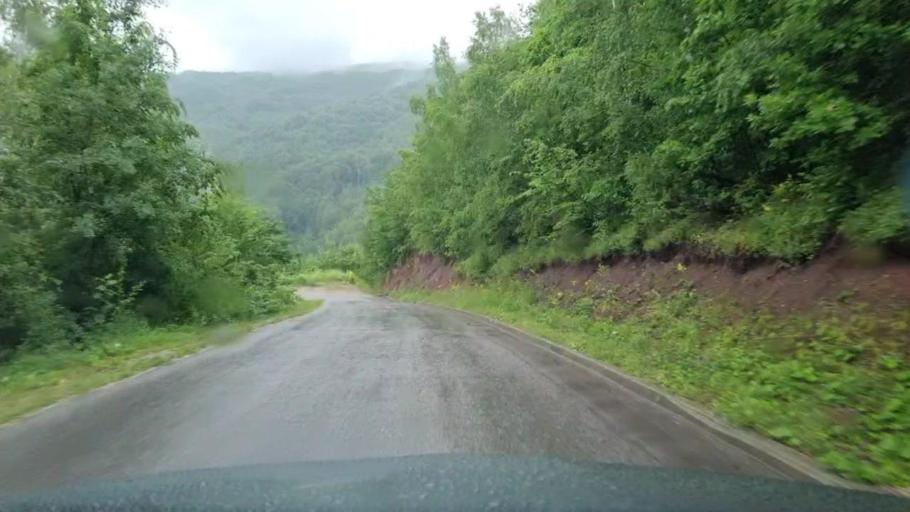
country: BA
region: Federation of Bosnia and Herzegovina
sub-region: Bosansko-Podrinjski Kanton
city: Ustikolina
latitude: 43.6316
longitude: 18.6248
